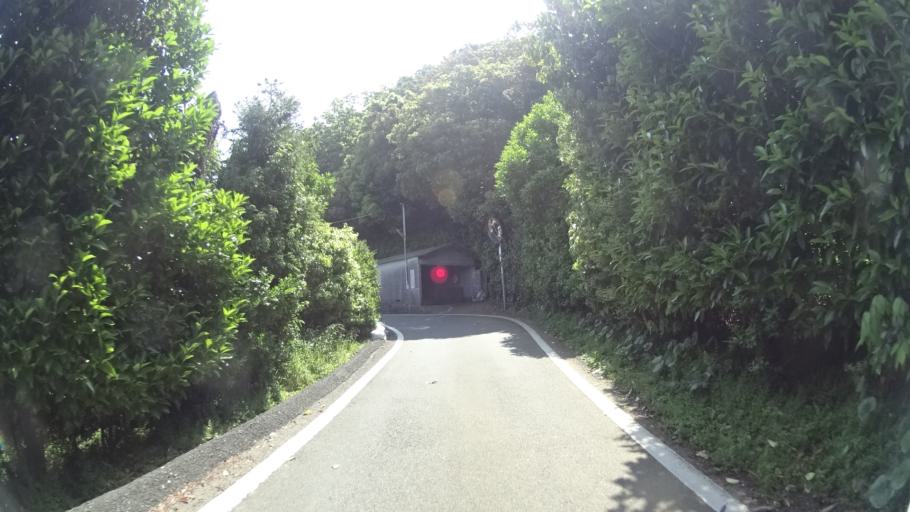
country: JP
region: Ehime
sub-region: Nishiuwa-gun
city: Ikata-cho
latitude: 33.3694
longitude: 132.0497
